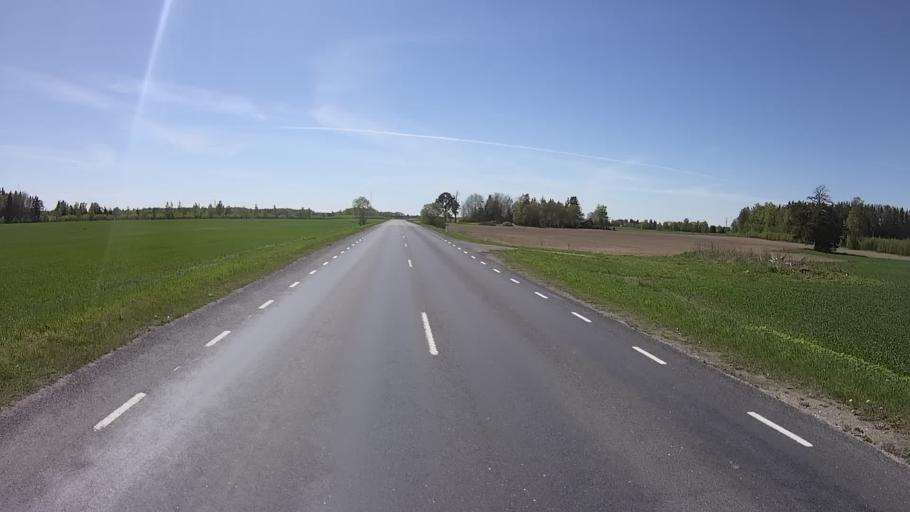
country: EE
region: Harju
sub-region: Raasiku vald
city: Raasiku
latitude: 59.1235
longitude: 25.1944
